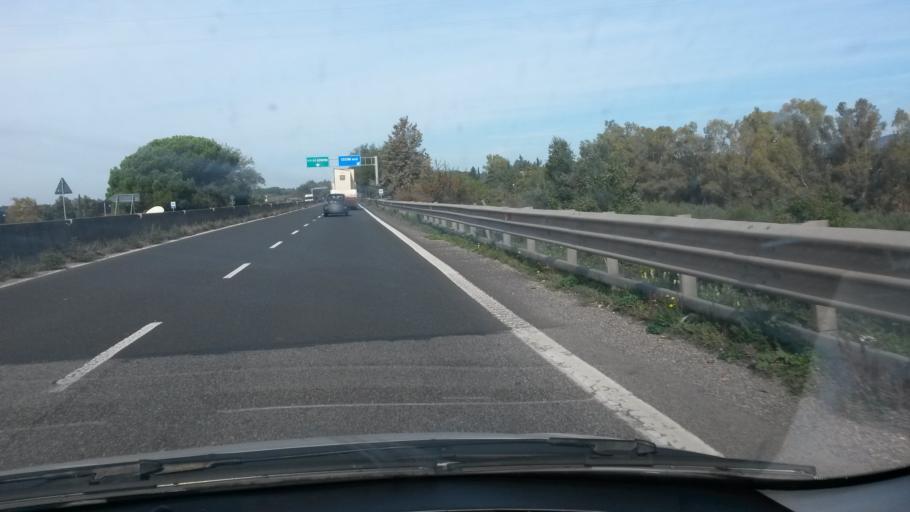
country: IT
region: Tuscany
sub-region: Provincia di Livorno
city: S.P. in Palazzi
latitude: 43.3301
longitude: 10.5269
